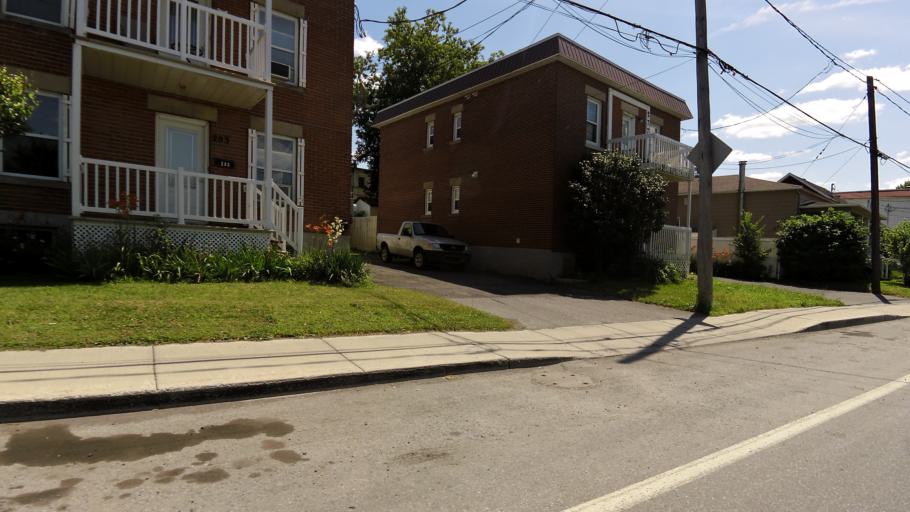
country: CA
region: Quebec
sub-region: Monteregie
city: Saint-Jean-sur-Richelieu
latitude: 45.3086
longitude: -73.2647
